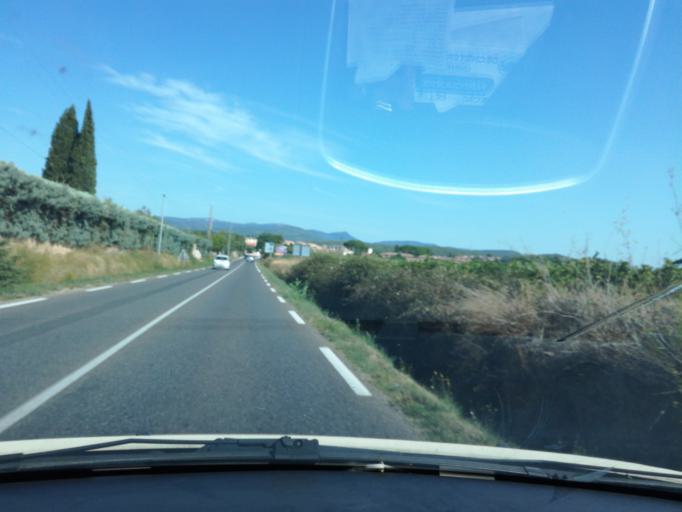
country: FR
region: Provence-Alpes-Cote d'Azur
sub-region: Departement du Var
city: La Crau
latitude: 43.1414
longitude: 6.0802
